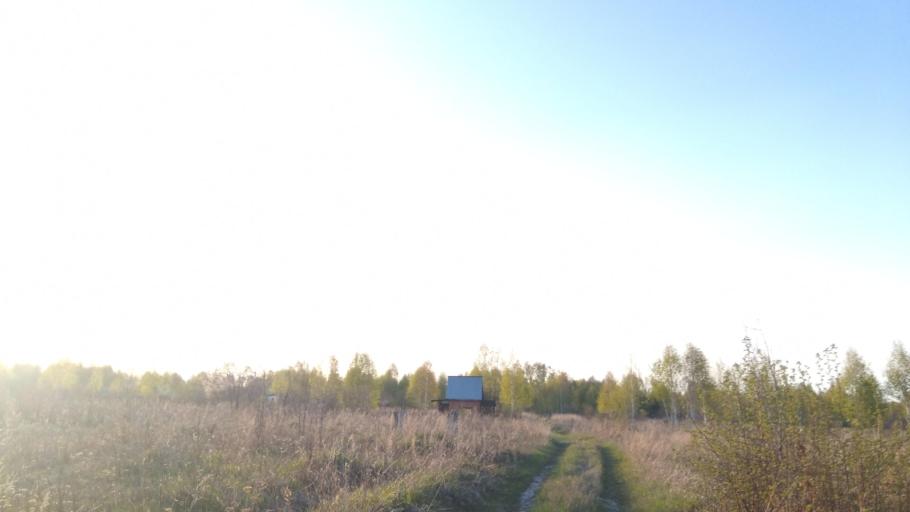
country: RU
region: Chelyabinsk
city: Timiryazevskiy
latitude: 54.9902
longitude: 60.8536
